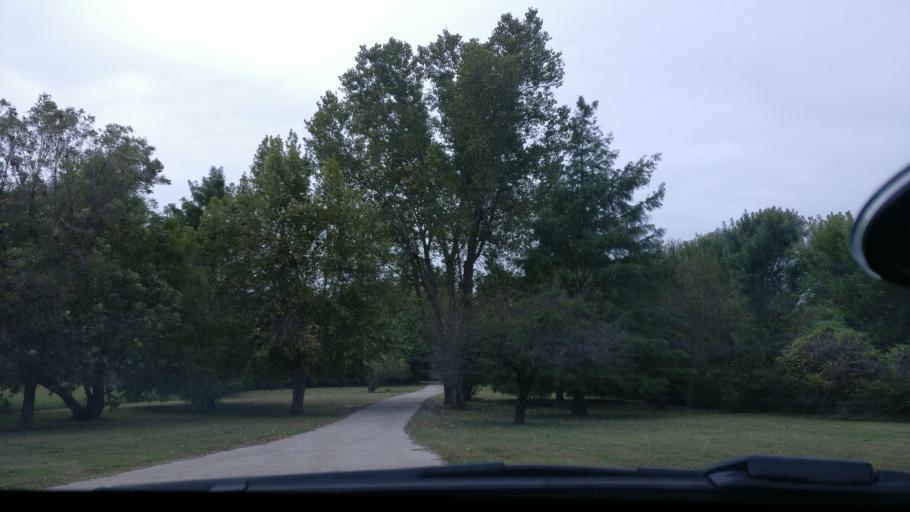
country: US
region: Oklahoma
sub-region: McClain County
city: Goldsby
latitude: 35.1906
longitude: -97.5362
